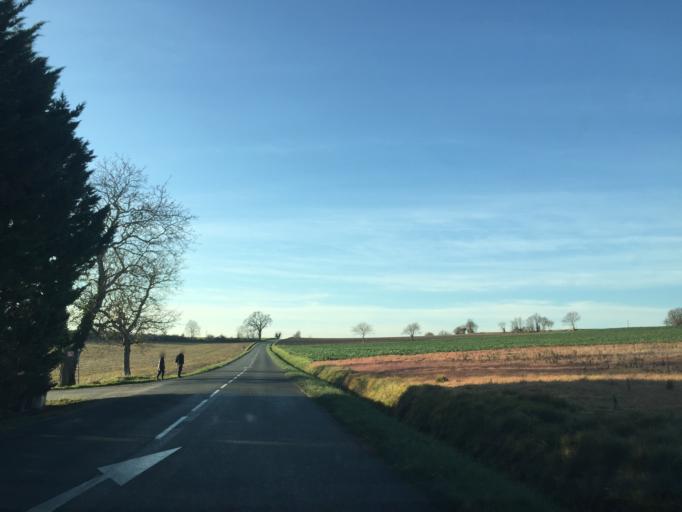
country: FR
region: Aquitaine
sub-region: Departement de la Dordogne
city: Saint-Aulaye
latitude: 45.2781
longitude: 0.1346
